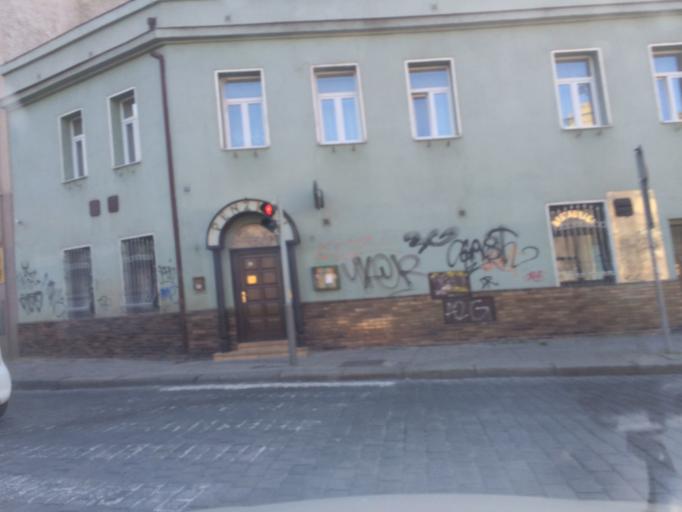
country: CZ
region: Praha
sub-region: Praha 8
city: Karlin
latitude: 50.0894
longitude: 14.4434
